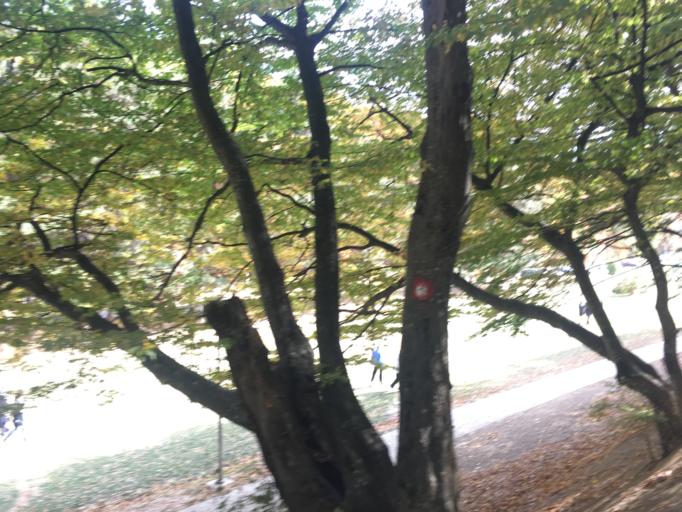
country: XK
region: Pristina
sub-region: Komuna e Prishtines
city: Pristina
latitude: 42.6736
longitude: 21.2141
